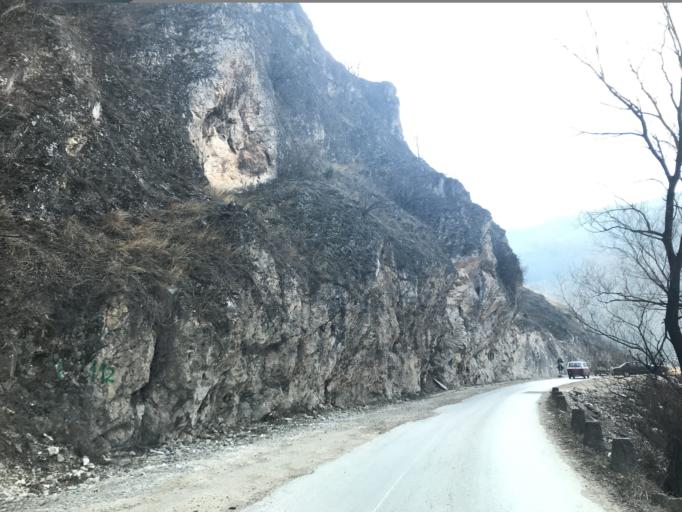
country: XK
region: Prizren
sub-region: Prizren
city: Prizren
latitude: 42.2085
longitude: 20.7519
